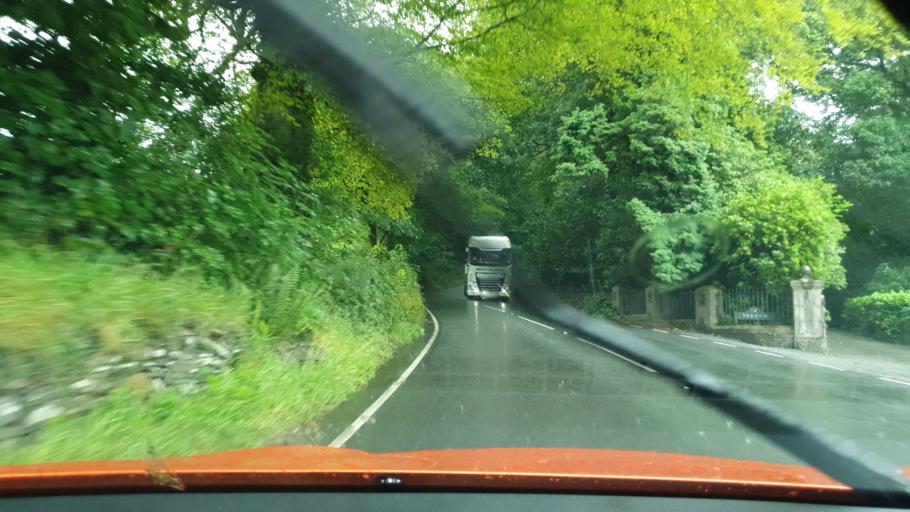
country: GB
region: England
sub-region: Cumbria
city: Ulverston
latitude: 54.2504
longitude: -3.0691
